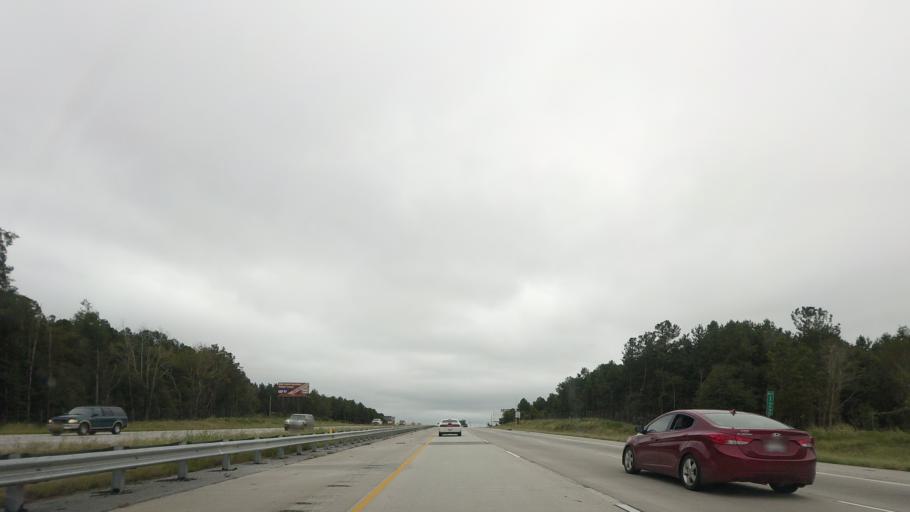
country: US
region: Georgia
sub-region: Dooly County
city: Unadilla
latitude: 32.2673
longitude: -83.7518
